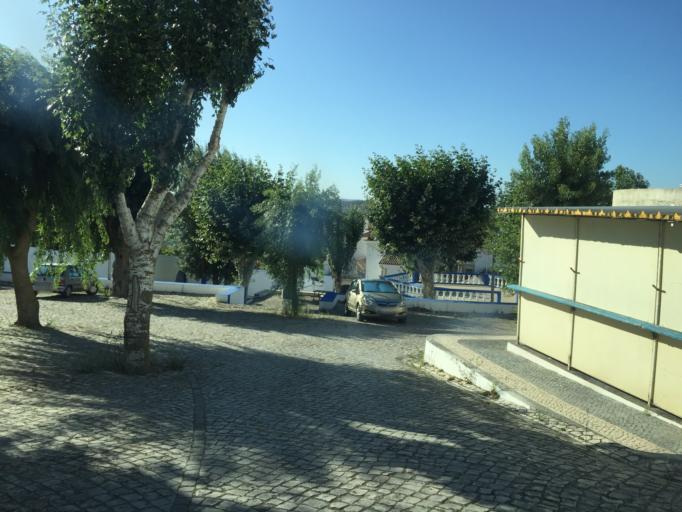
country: PT
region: Lisbon
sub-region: Torres Vedras
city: Torres Vedras
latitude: 39.0900
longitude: -9.2792
